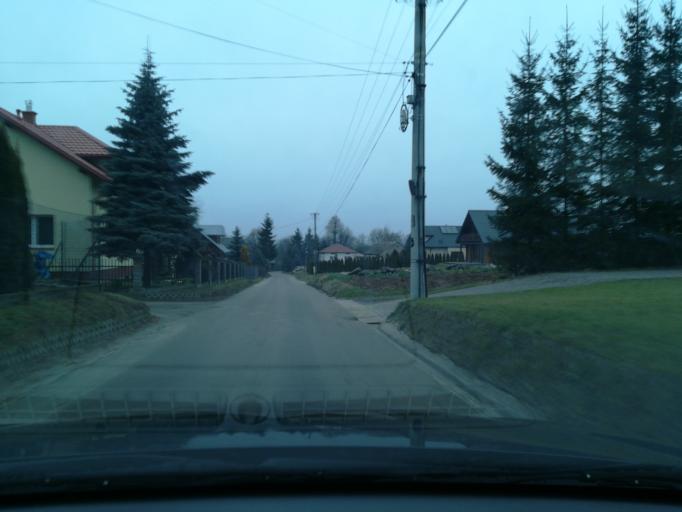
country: PL
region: Subcarpathian Voivodeship
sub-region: Powiat lancucki
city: Kosina
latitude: 50.0772
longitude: 22.3359
